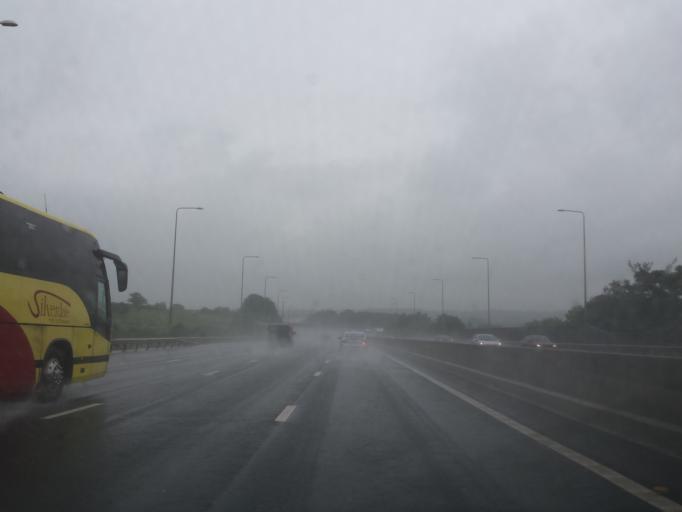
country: GB
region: England
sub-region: Nottinghamshire
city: Kimberley
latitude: 52.9543
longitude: -1.2749
